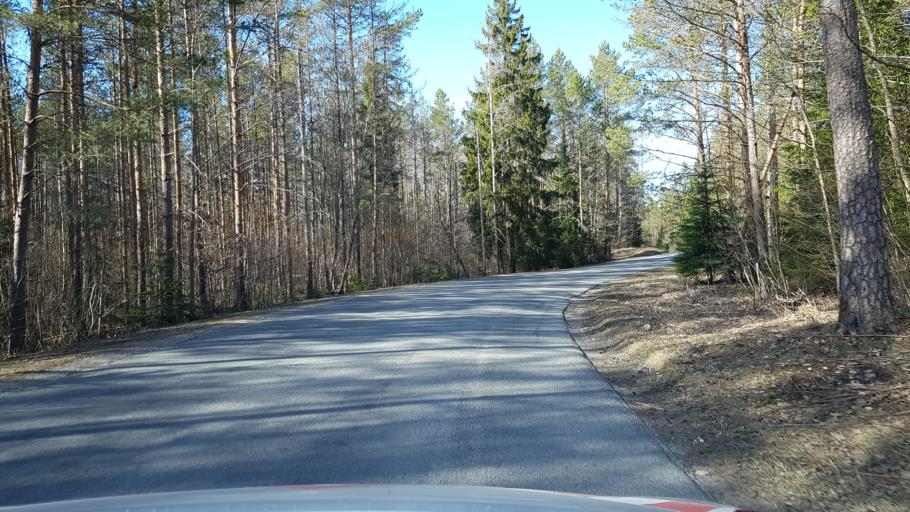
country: EE
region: Harju
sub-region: Nissi vald
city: Riisipere
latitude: 59.0835
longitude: 24.3541
